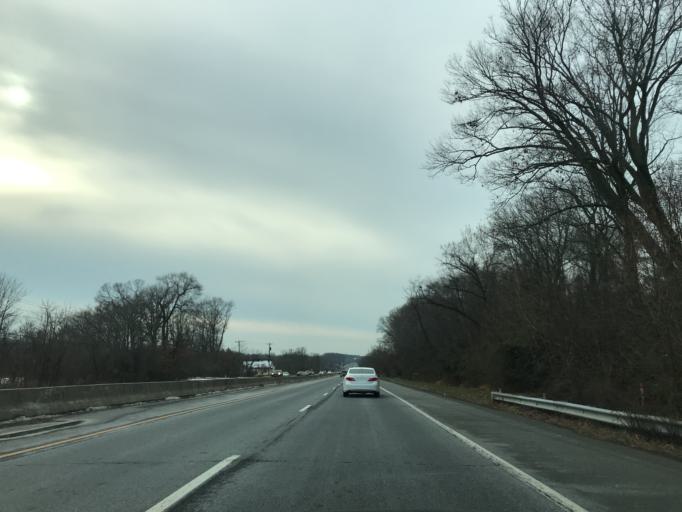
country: US
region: Maryland
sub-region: Harford County
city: Riverside
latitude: 39.4668
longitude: -76.2428
